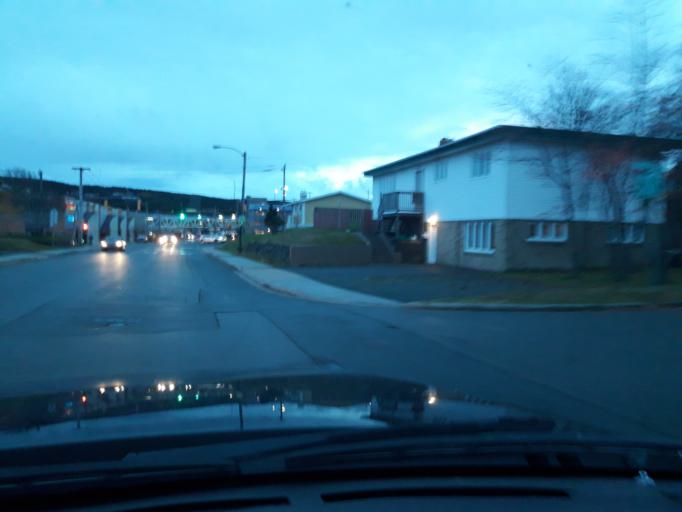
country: CA
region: Newfoundland and Labrador
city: St. John's
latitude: 47.5634
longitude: -52.7551
